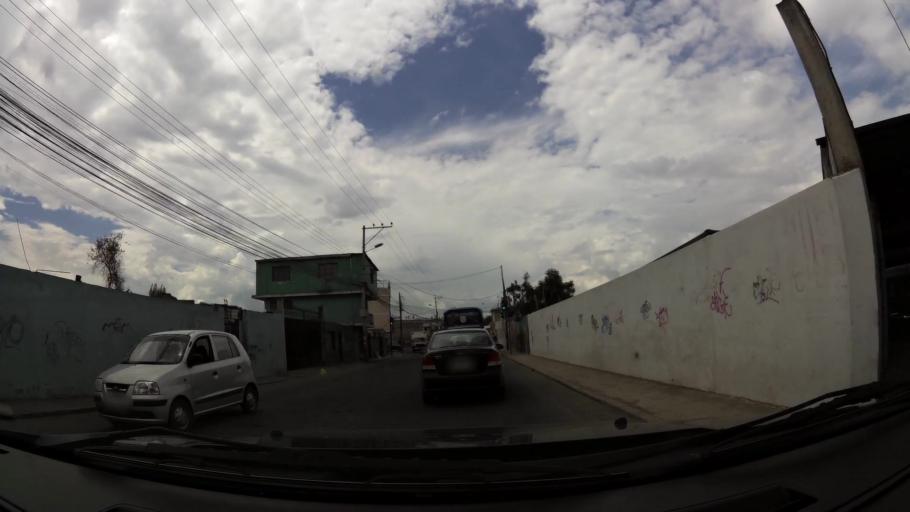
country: EC
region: Pichincha
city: Quito
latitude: -0.0845
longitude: -78.4193
